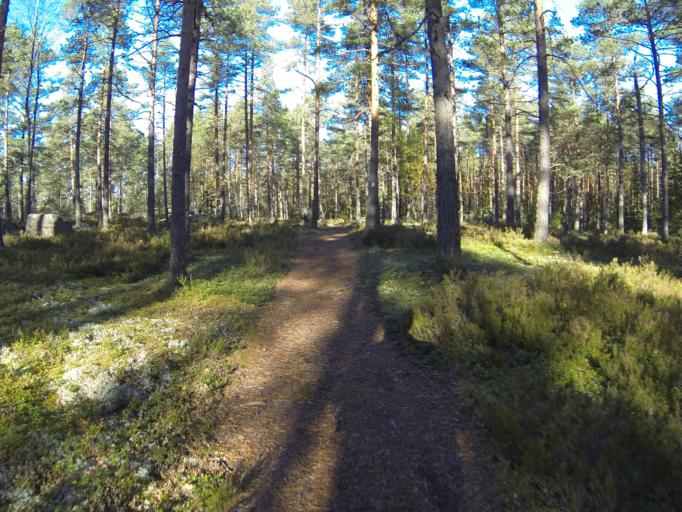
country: FI
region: Varsinais-Suomi
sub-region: Salo
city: Saerkisalo
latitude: 60.2045
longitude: 22.9221
